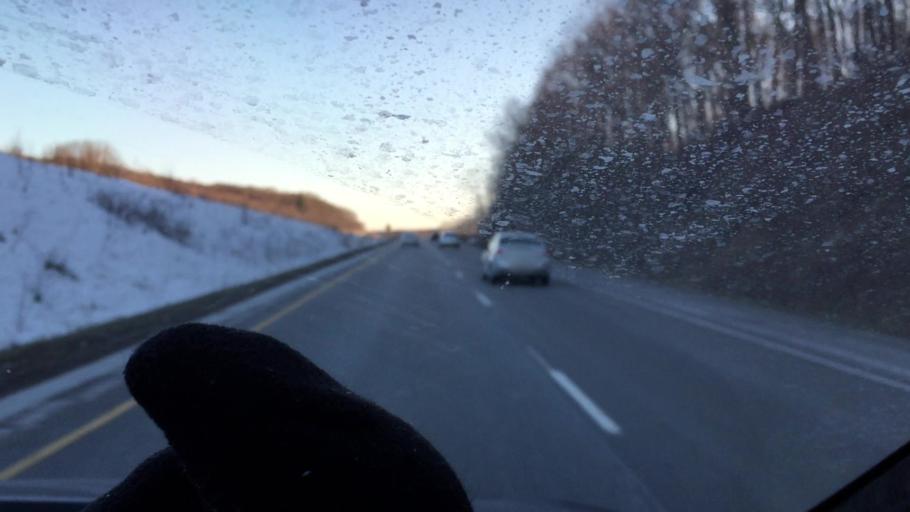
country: US
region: Pennsylvania
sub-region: Crawford County
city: Meadville
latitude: 41.6863
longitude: -80.2060
